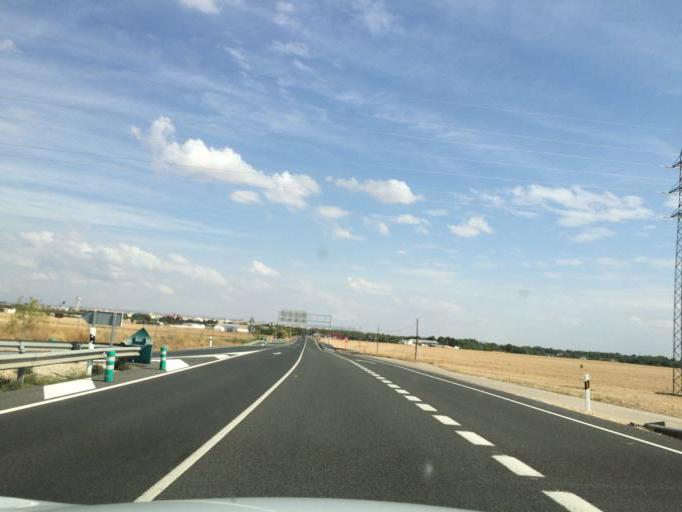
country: ES
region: Castille-La Mancha
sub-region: Provincia de Albacete
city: Albacete
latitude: 39.0009
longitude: -1.9014
